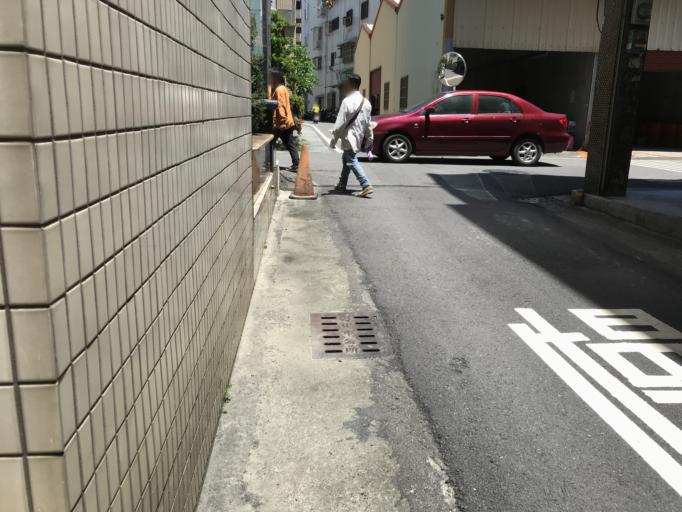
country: TW
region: Taiwan
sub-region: Changhua
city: Chang-hua
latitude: 24.0680
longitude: 120.5289
